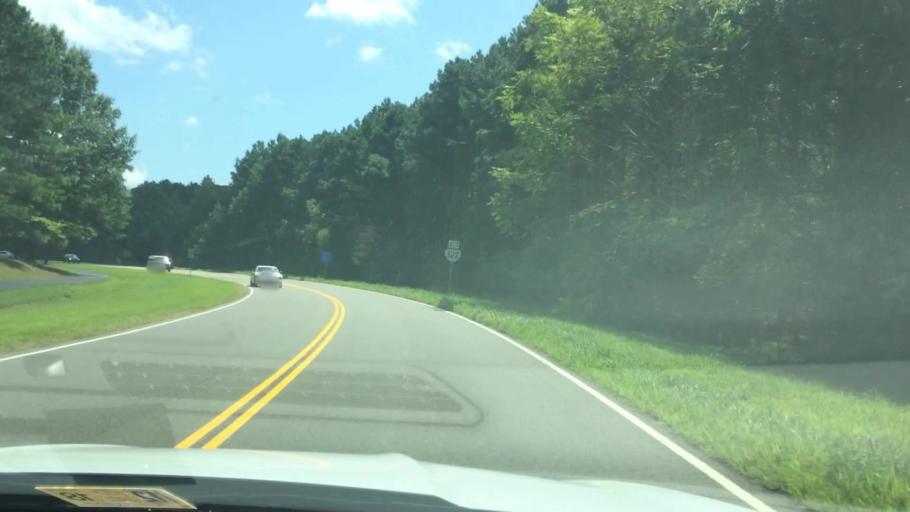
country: US
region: Virginia
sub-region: James City County
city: Williamsburg
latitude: 37.2963
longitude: -76.7398
